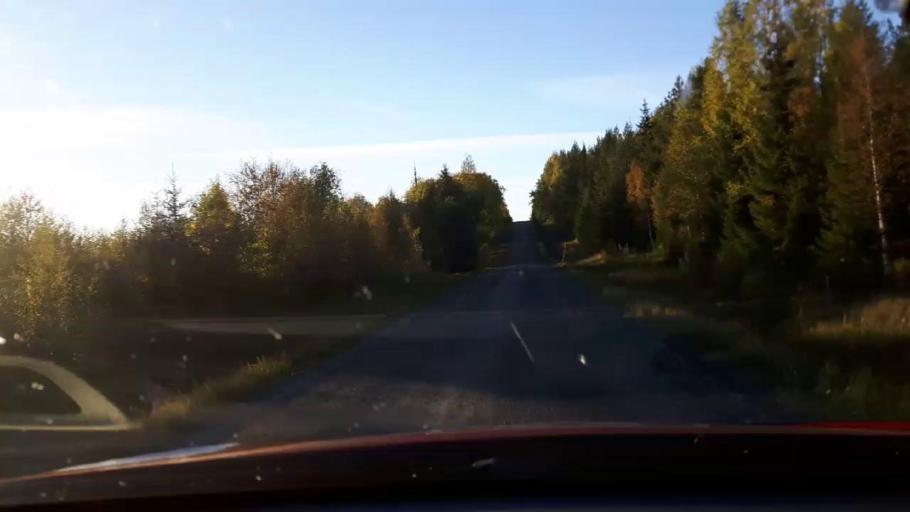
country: SE
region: Jaemtland
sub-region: Krokoms Kommun
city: Krokom
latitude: 63.4138
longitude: 14.6215
